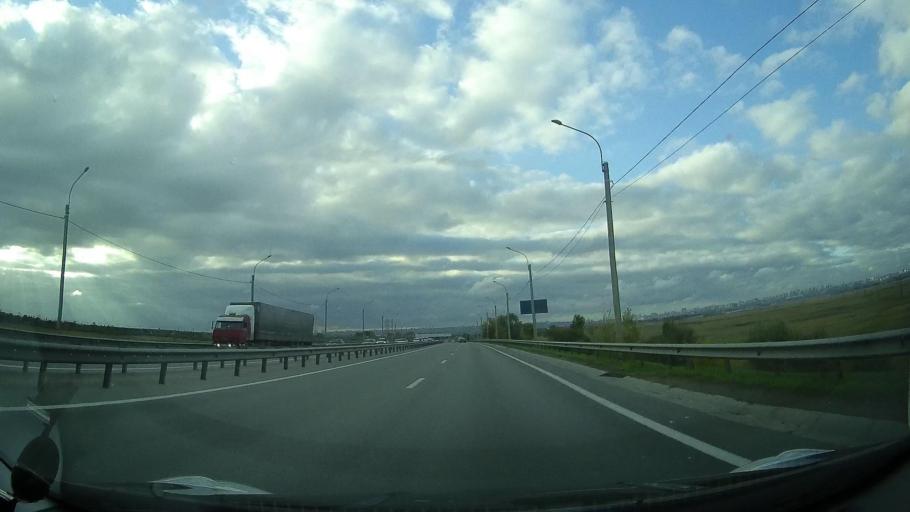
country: RU
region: Rostov
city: Bataysk
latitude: 47.1661
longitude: 39.7554
